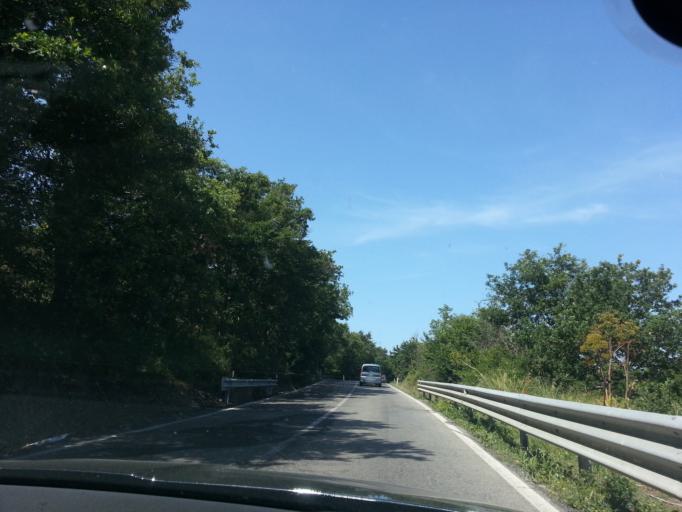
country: IT
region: Latium
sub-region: Provincia di Viterbo
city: Monte Romano
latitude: 42.2625
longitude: 11.8502
